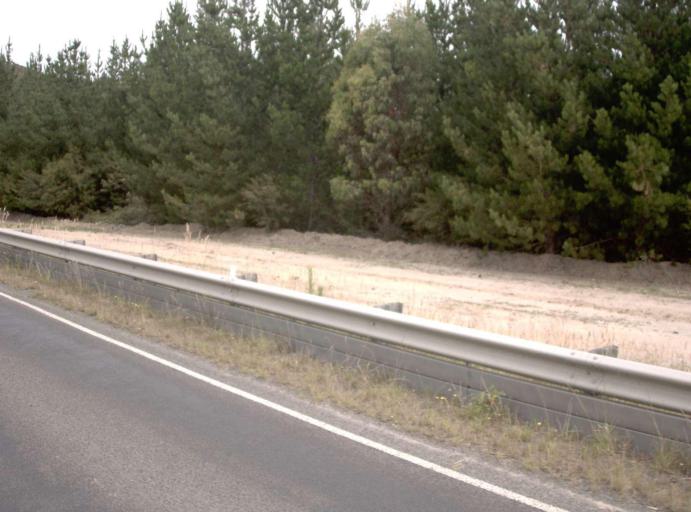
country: AU
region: Victoria
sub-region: Latrobe
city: Traralgon
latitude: -38.1201
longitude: 146.4582
